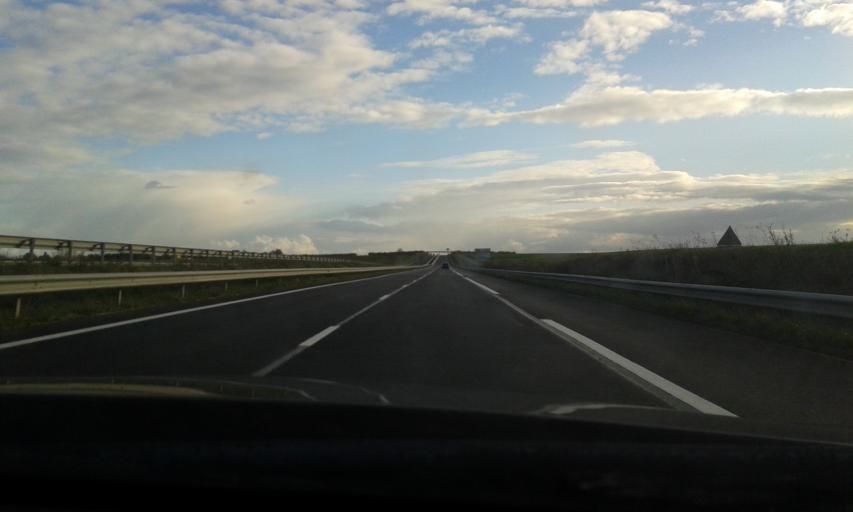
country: FR
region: Centre
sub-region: Departement d'Eure-et-Loir
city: Leves
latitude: 48.5184
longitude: 1.4588
